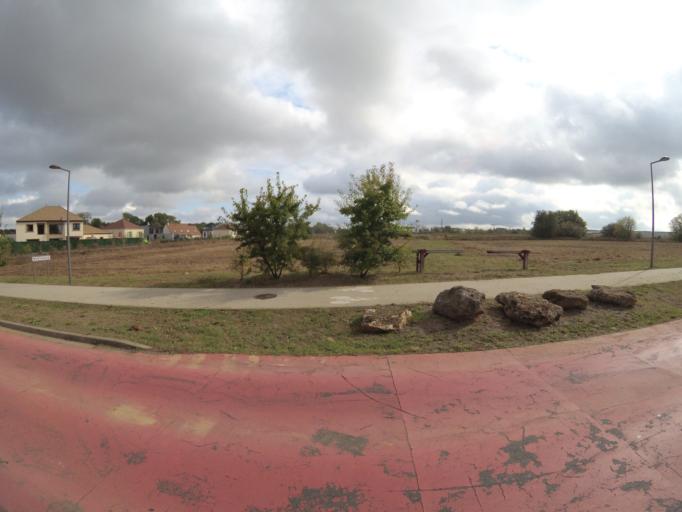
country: FR
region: Ile-de-France
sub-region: Departement de Seine-et-Marne
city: Montevrain
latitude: 48.8645
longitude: 2.7533
